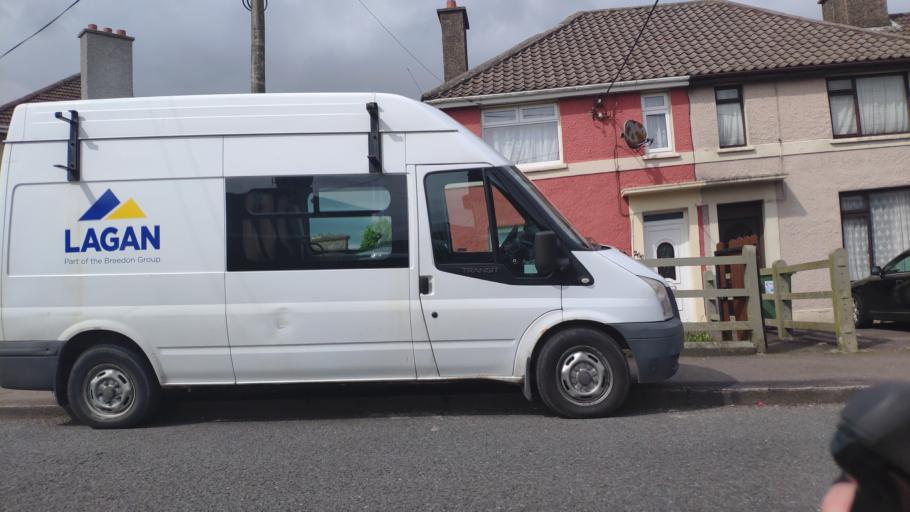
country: IE
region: Munster
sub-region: County Cork
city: Cork
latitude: 51.9036
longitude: -8.4935
